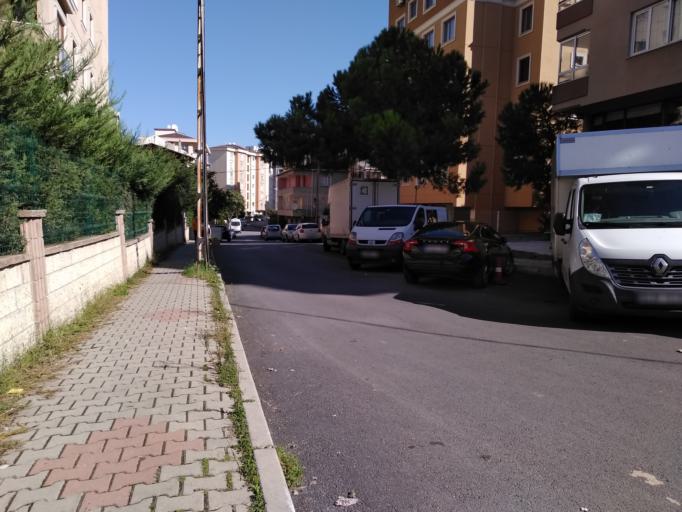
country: TR
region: Istanbul
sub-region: Atasehir
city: Atasehir
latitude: 40.9793
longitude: 29.1199
